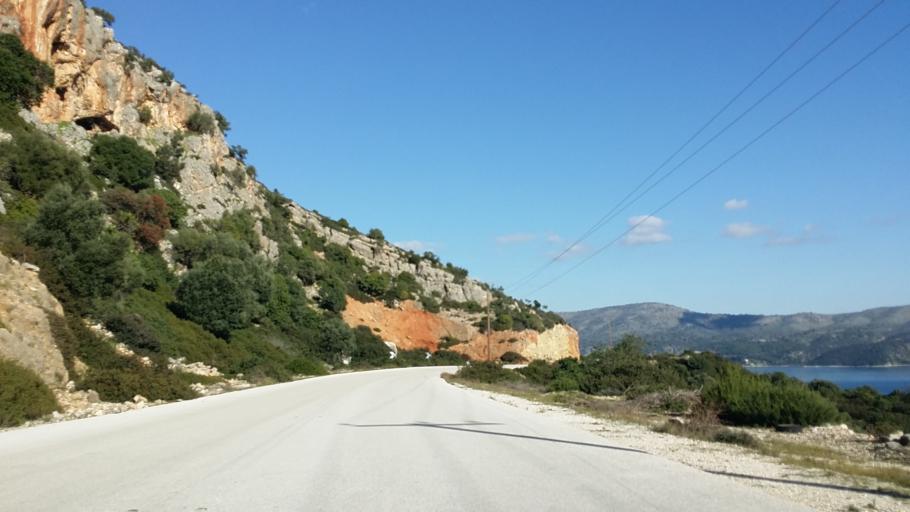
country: GR
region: West Greece
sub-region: Nomos Aitolias kai Akarnanias
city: Astakos
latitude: 38.5143
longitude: 21.0516
